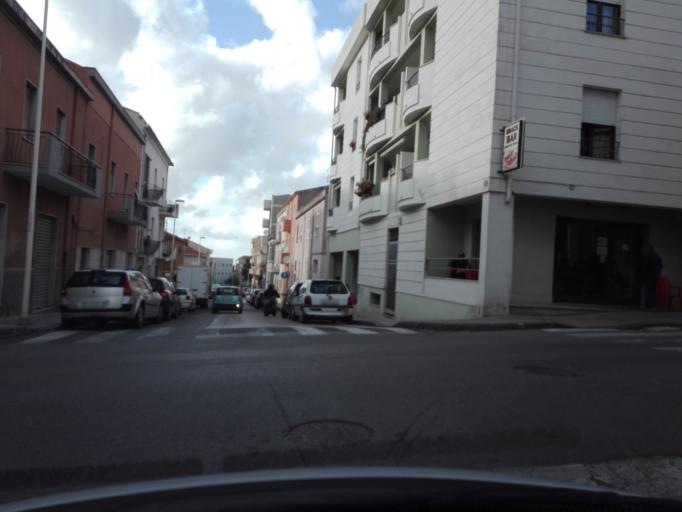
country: IT
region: Sardinia
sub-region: Provincia di Sassari
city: Sassari
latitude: 40.7339
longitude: 8.5656
